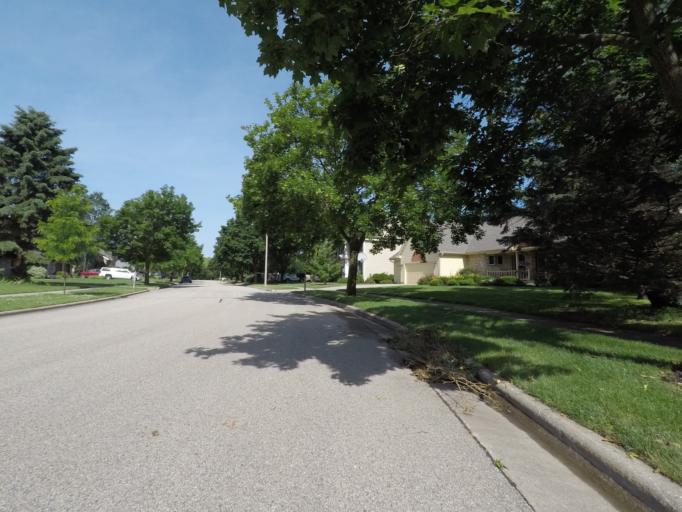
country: US
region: Wisconsin
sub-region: Dane County
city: Middleton
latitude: 43.0820
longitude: -89.4940
